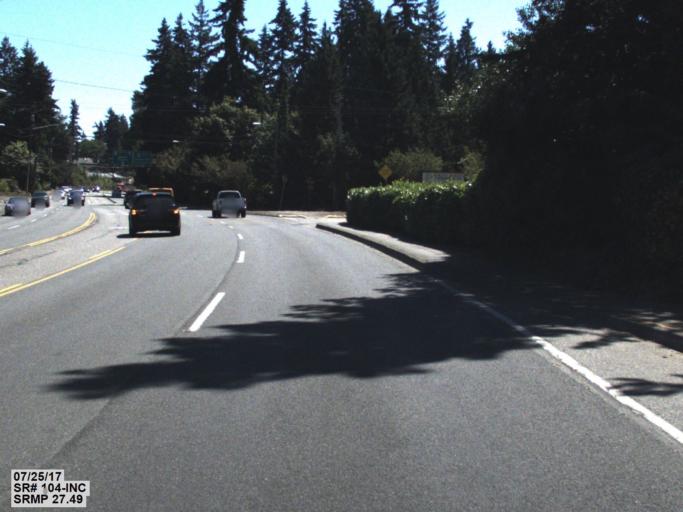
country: US
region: Washington
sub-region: Snohomish County
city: Esperance
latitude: 47.7838
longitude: -122.3525
